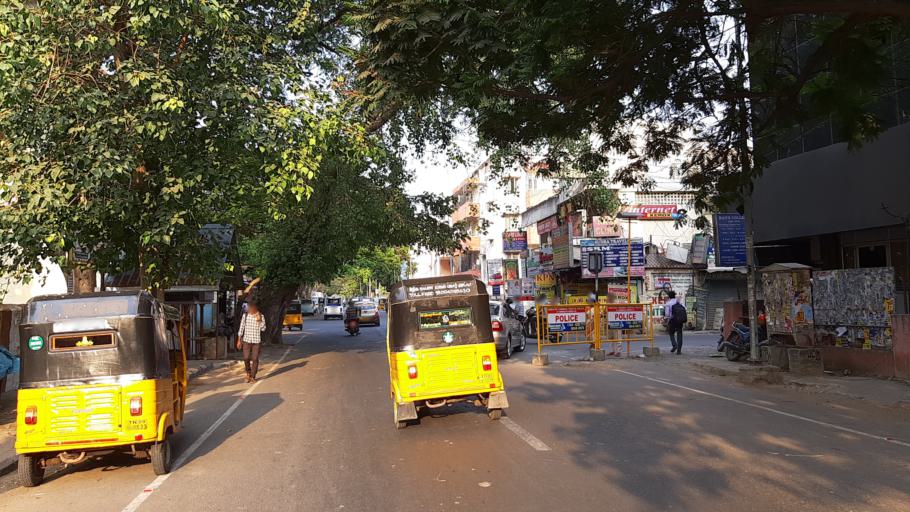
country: IN
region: Tamil Nadu
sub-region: Chennai
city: Gandhi Nagar
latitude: 13.0347
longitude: 80.2329
